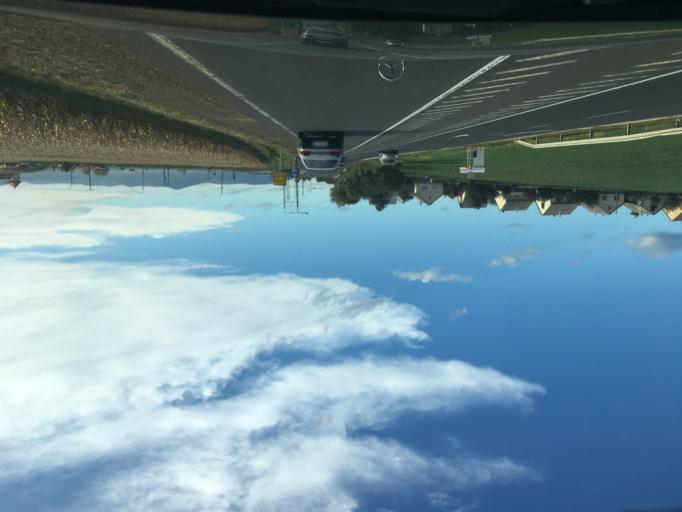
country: HU
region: Borsod-Abauj-Zemplen
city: Encs
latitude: 48.3344
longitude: 21.1042
